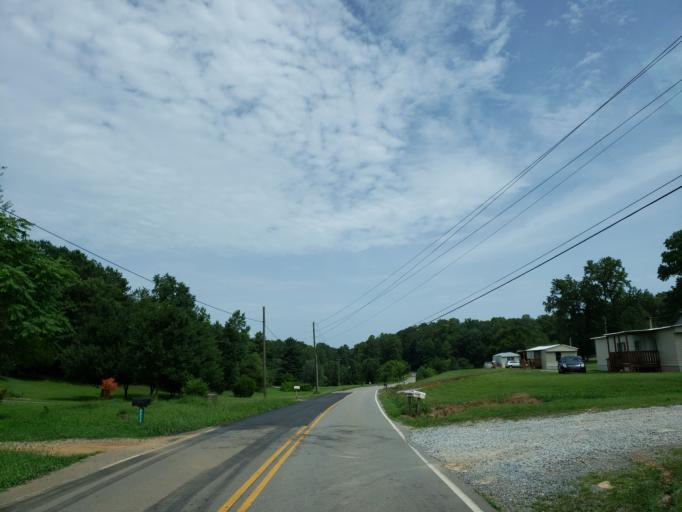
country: US
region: Georgia
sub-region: Pickens County
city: Jasper
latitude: 34.4514
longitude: -84.4407
